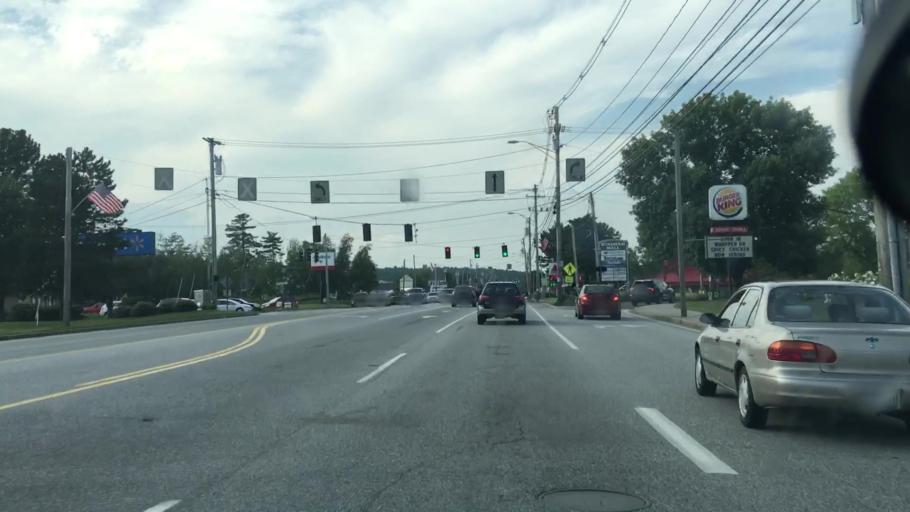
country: US
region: Maine
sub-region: Cumberland County
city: North Windham
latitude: 43.8386
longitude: -70.4420
